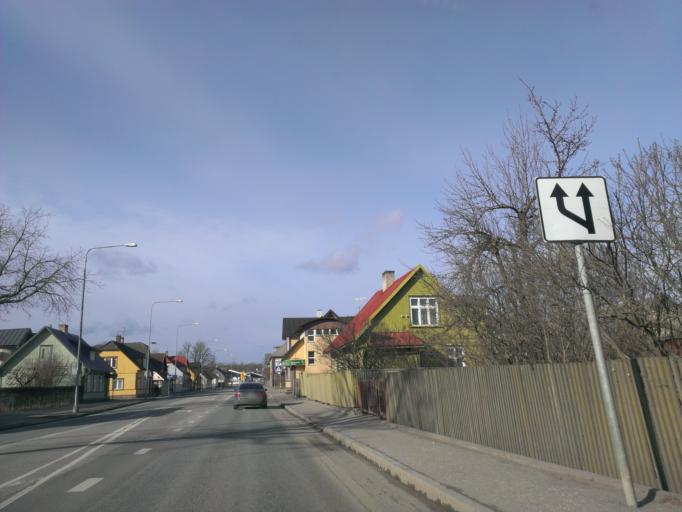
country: EE
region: Paernumaa
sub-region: Paernu linn
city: Parnu
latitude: 58.4005
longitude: 24.4931
